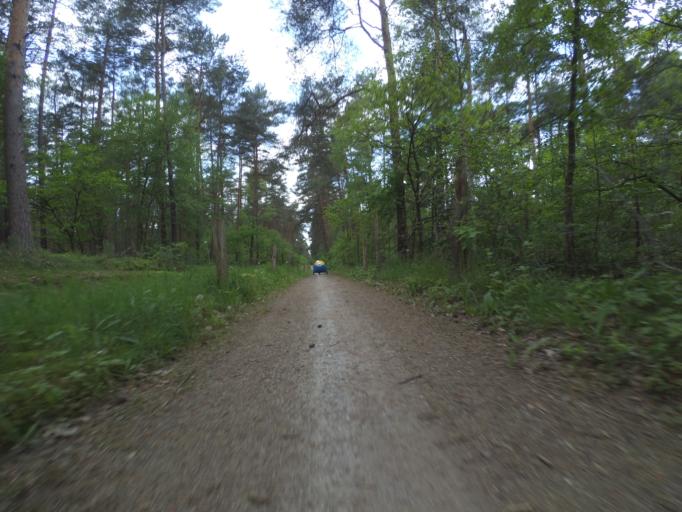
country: DE
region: Lower Saxony
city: Wietze
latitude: 52.6630
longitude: 9.7985
